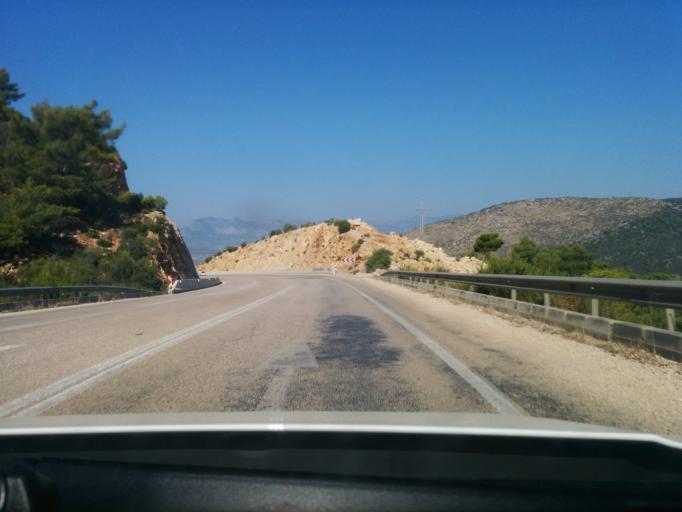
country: TR
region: Antalya
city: Kalkan
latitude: 36.2780
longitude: 29.3897
